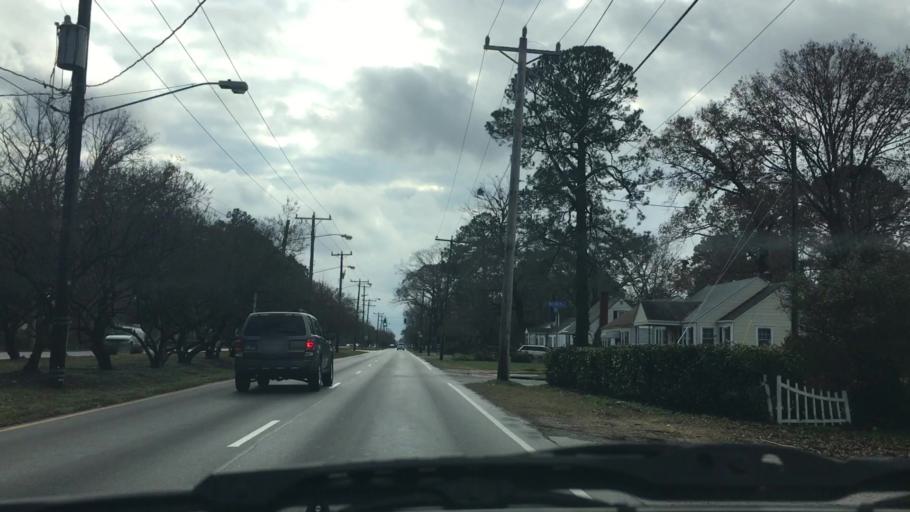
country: US
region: Virginia
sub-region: City of Norfolk
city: Norfolk
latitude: 36.9251
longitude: -76.2432
